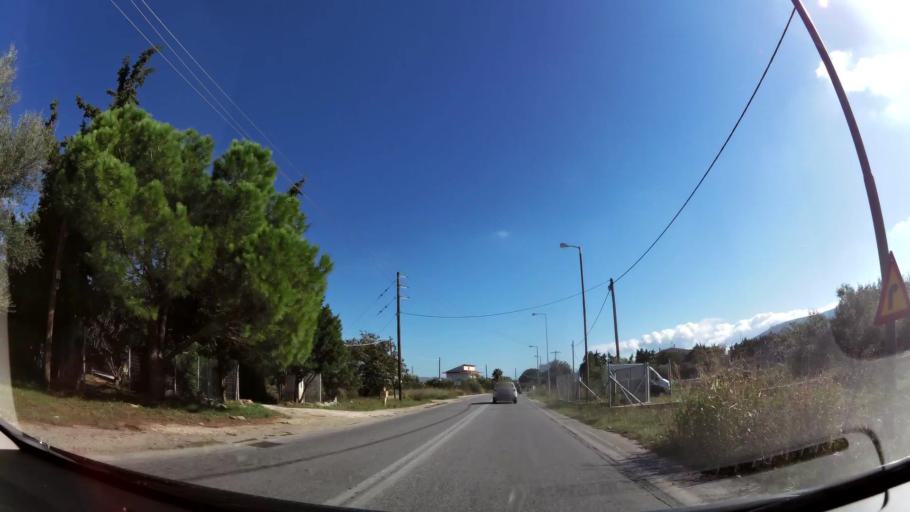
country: GR
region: Attica
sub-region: Nomarchia Anatolikis Attikis
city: Markopoulo
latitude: 37.8868
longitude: 23.9080
